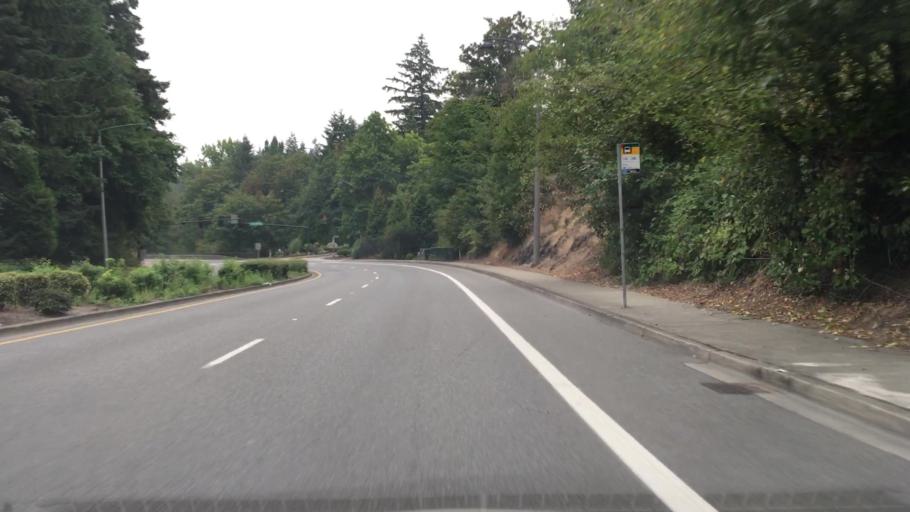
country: US
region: Washington
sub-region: King County
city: Newcastle
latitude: 47.5287
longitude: -122.1633
